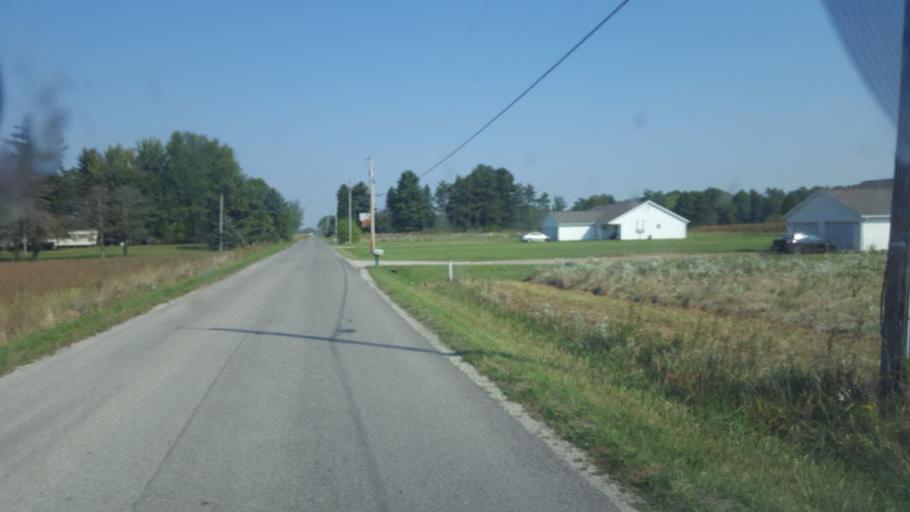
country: US
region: Ohio
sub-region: Crawford County
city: Galion
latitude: 40.6719
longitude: -82.7843
